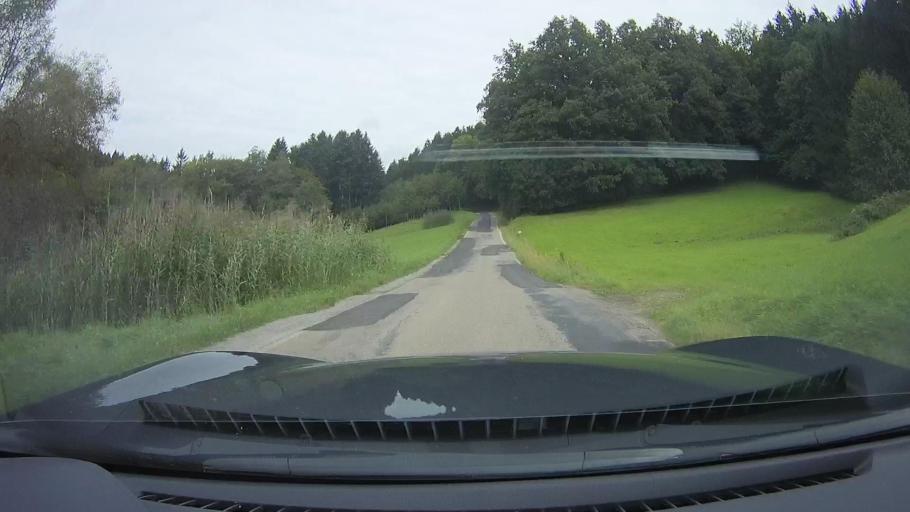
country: DE
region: Baden-Wuerttemberg
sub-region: Regierungsbezirk Stuttgart
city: Sulzbach an der Murr
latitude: 49.0003
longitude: 9.5372
